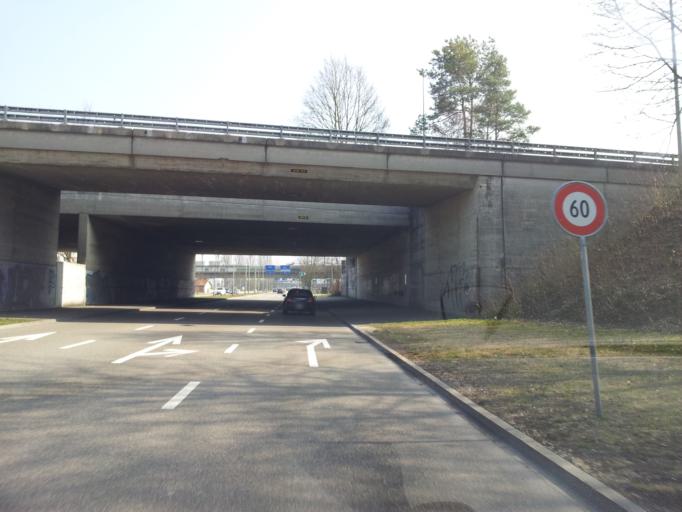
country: CH
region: Zurich
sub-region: Bezirk Buelach
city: Wallisellen / Wallisellen-Ost
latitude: 47.4035
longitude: 8.5987
